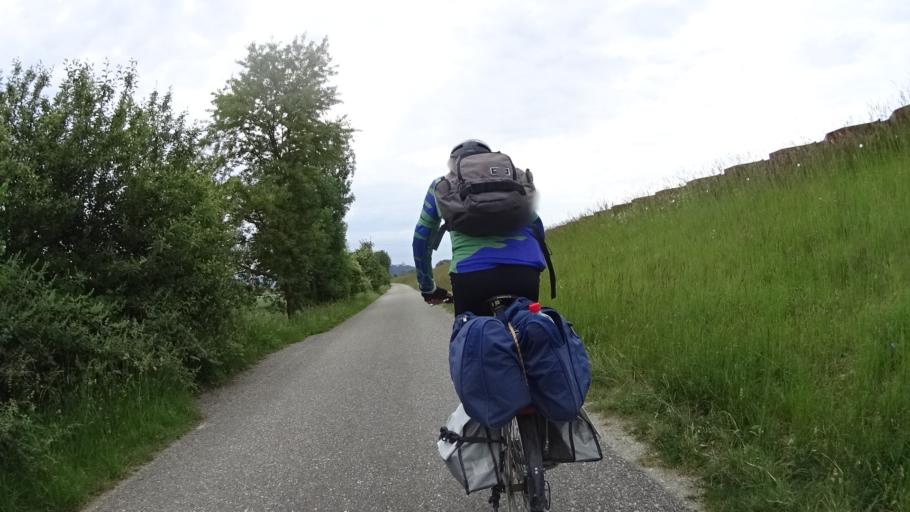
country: DE
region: Bavaria
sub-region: Lower Bavaria
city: Parkstetten
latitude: 48.9097
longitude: 12.6351
